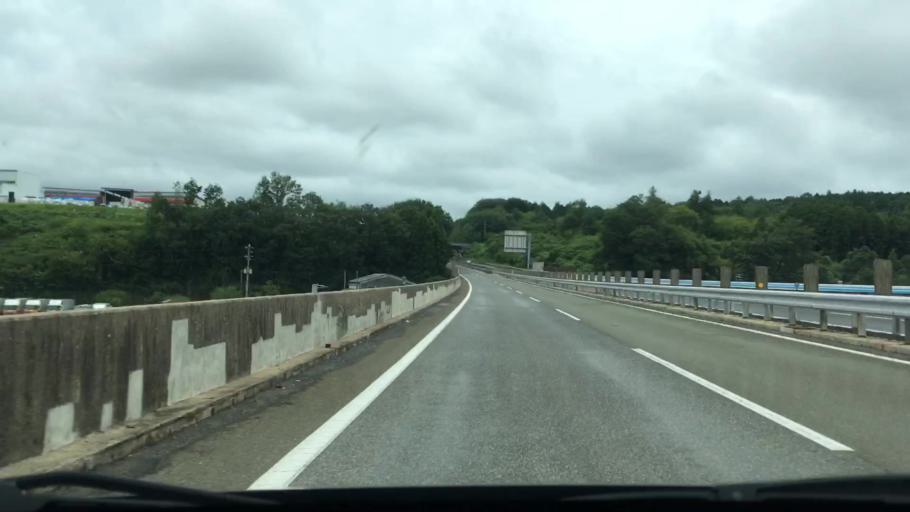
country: JP
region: Hiroshima
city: Miyoshi
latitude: 34.7960
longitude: 132.8893
